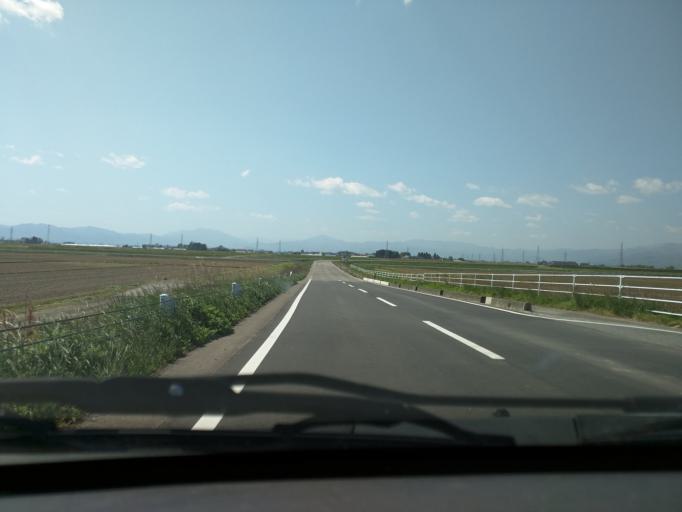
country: JP
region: Fukushima
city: Kitakata
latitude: 37.5857
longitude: 139.8698
